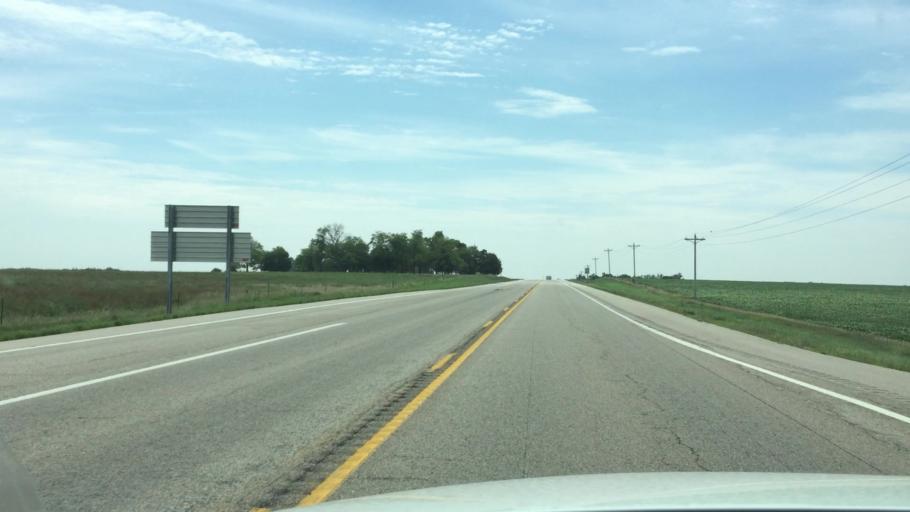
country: US
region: Kansas
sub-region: Nemaha County
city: Sabetha
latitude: 39.7536
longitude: -95.7297
